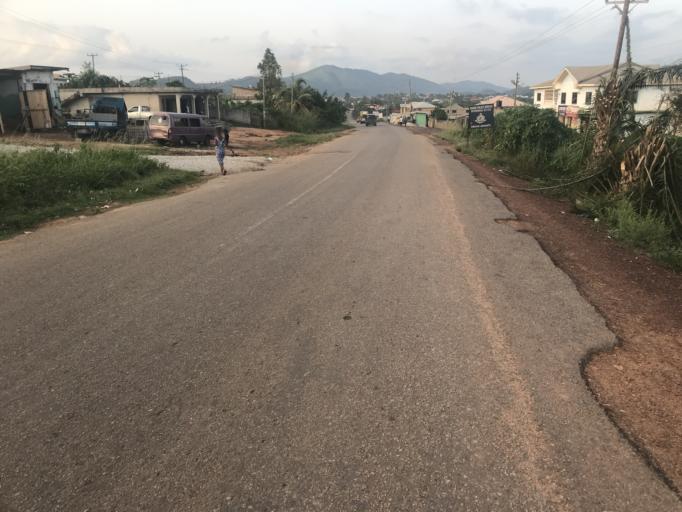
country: GH
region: Ashanti
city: Obuasi
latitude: 6.2045
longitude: -1.6022
